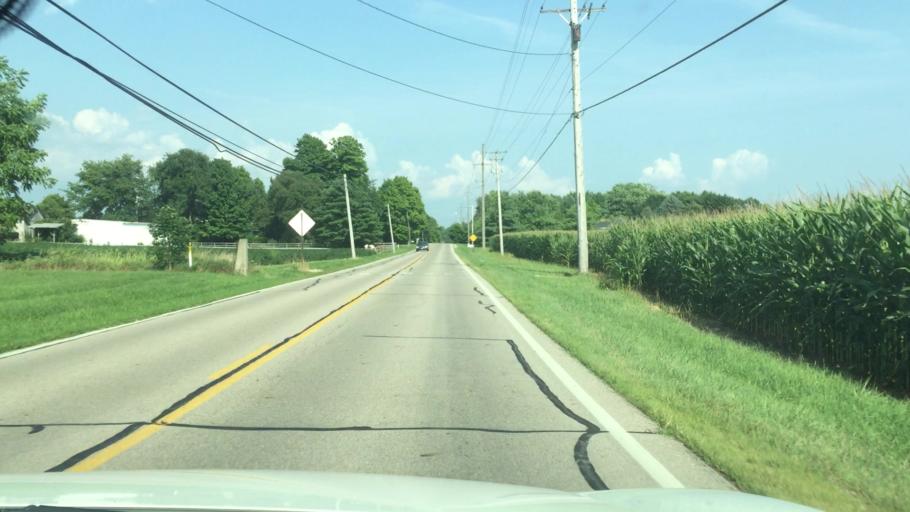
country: US
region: Ohio
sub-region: Clark County
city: Northridge
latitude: 39.9940
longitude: -83.7479
